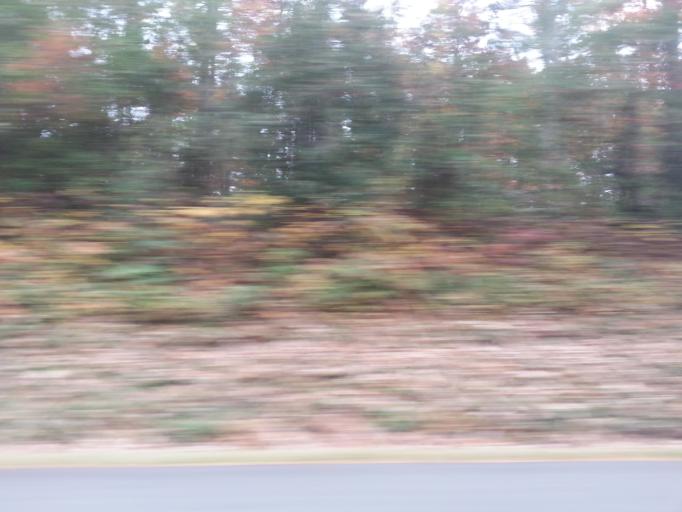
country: US
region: North Carolina
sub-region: Ashe County
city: Jefferson
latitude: 36.3501
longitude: -81.3731
